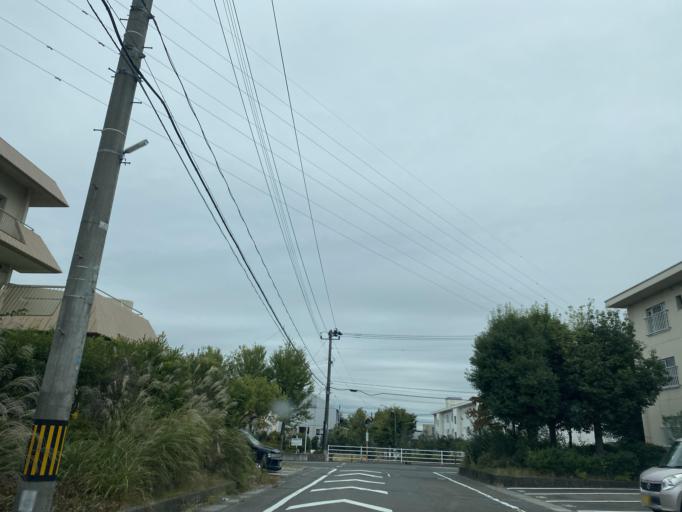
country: JP
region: Fukushima
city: Koriyama
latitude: 37.3739
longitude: 140.3530
